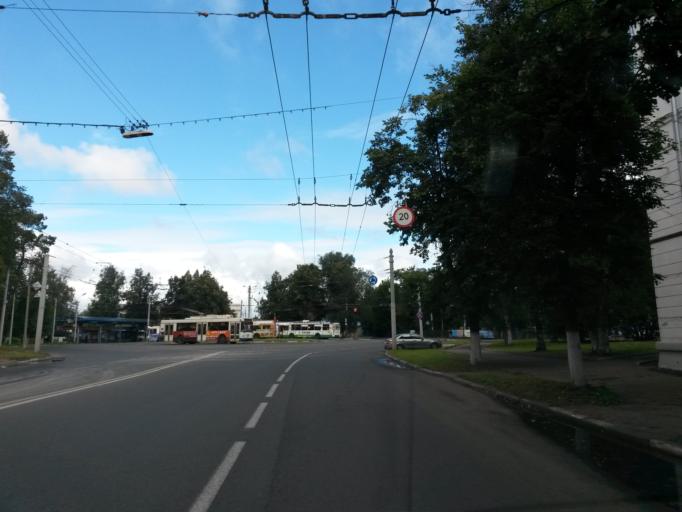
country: RU
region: Jaroslavl
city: Yaroslavl
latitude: 57.6419
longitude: 39.8747
